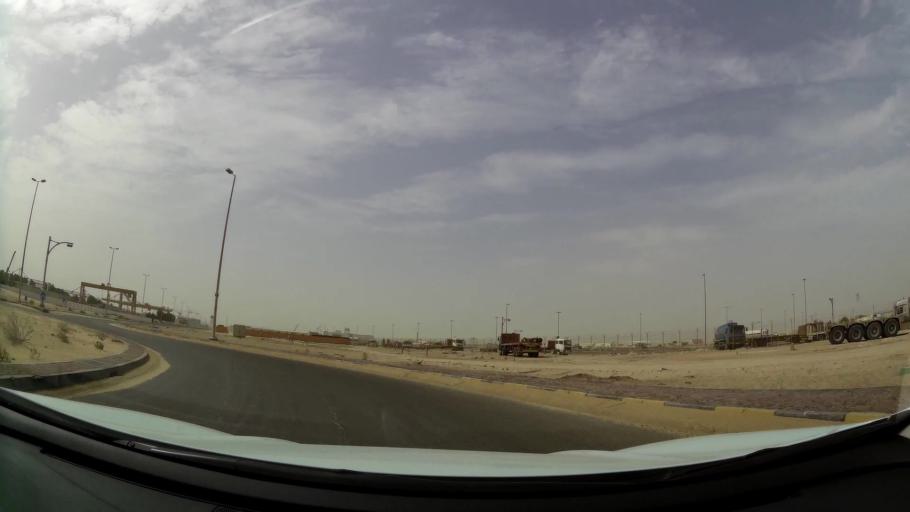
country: AE
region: Abu Dhabi
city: Abu Dhabi
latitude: 24.3357
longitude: 54.5036
